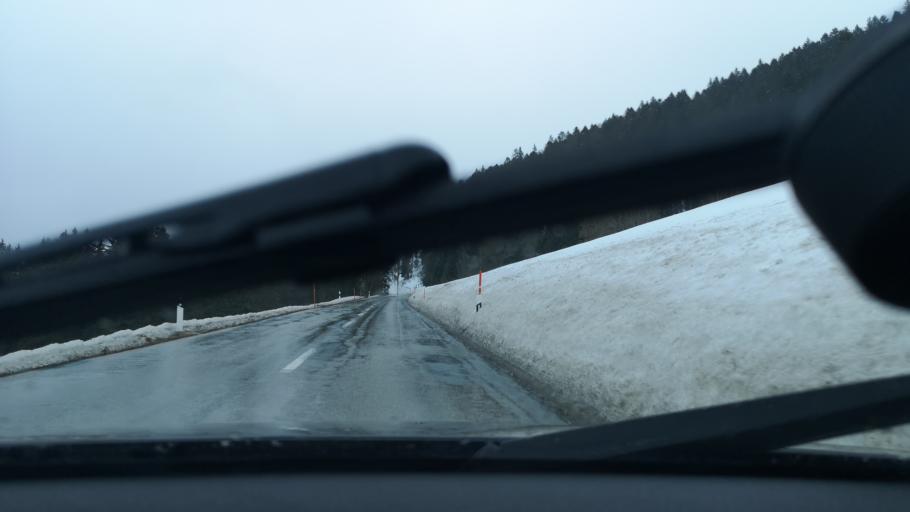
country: CH
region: Vaud
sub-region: Jura-Nord vaudois District
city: Sainte-Croix
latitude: 46.8262
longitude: 6.4855
